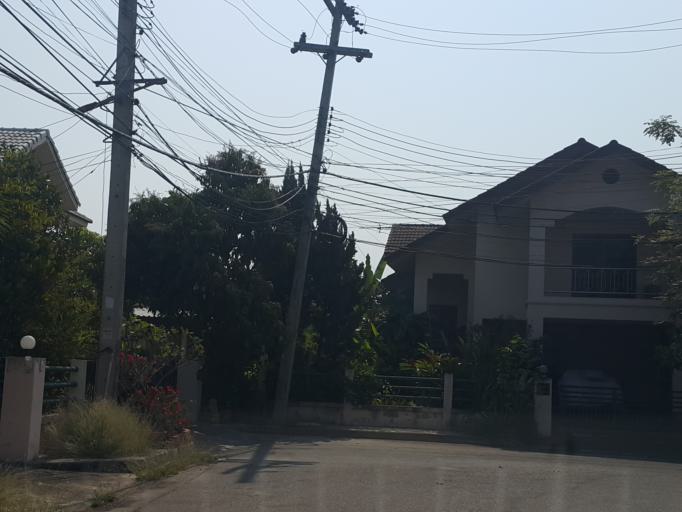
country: TH
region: Chiang Mai
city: Hang Dong
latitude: 18.7181
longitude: 98.9632
